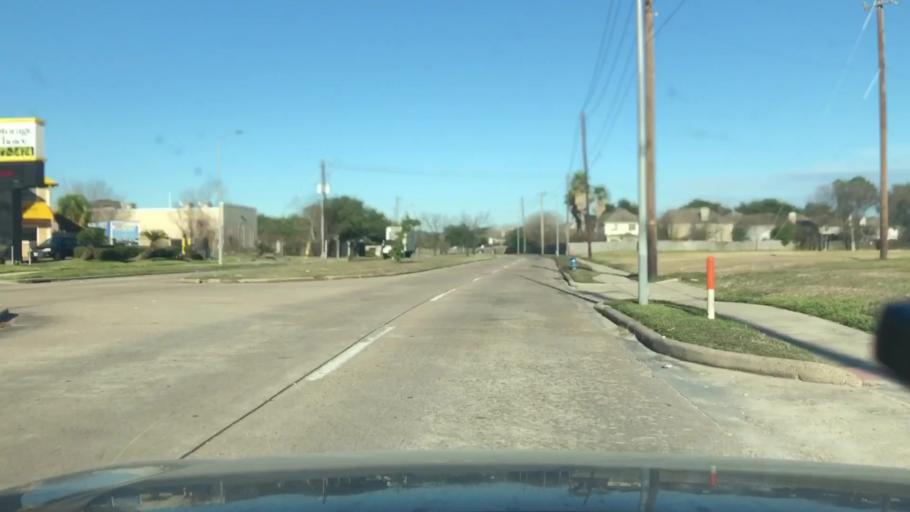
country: US
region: Texas
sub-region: Fort Bend County
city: Missouri City
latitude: 29.6432
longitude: -95.5299
